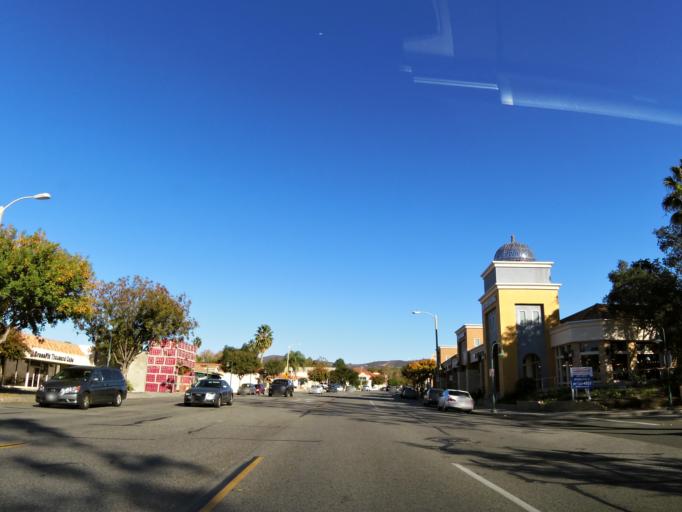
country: US
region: California
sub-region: Ventura County
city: Thousand Oaks
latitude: 34.1793
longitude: -118.8648
